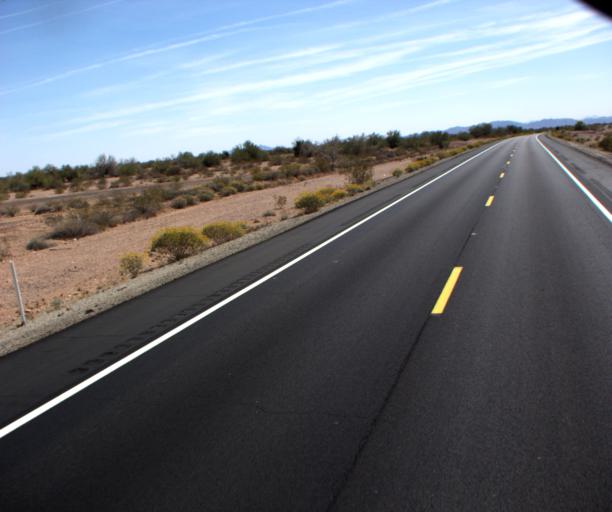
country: US
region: Arizona
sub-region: Yuma County
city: Wellton
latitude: 33.0120
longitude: -114.2856
